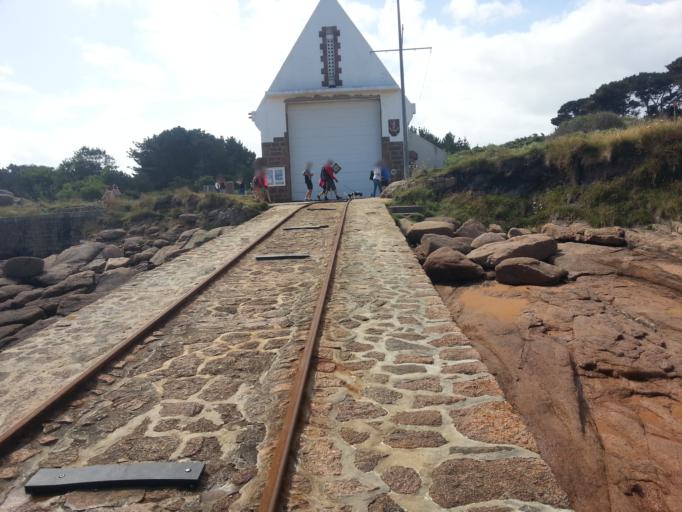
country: FR
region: Brittany
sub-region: Departement des Cotes-d'Armor
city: Tregastel
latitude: 48.8366
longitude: -3.4816
